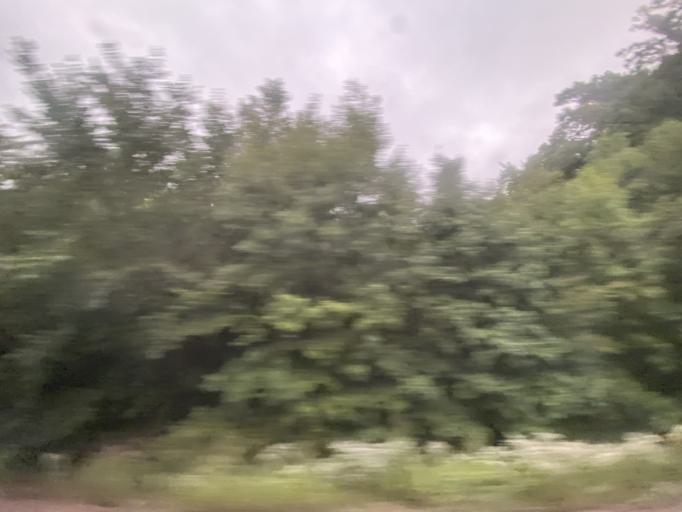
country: US
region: Indiana
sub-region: LaPorte County
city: Westville
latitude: 41.5973
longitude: -86.9216
